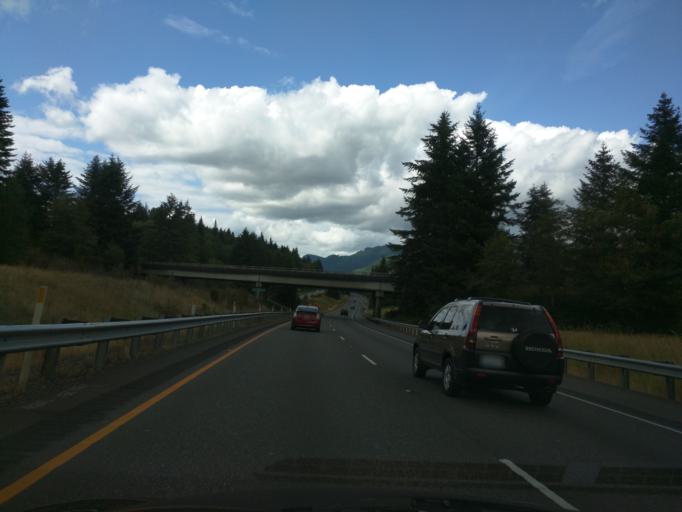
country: US
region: Washington
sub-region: Whatcom County
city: Sudden Valley
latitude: 48.6204
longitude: -122.3561
